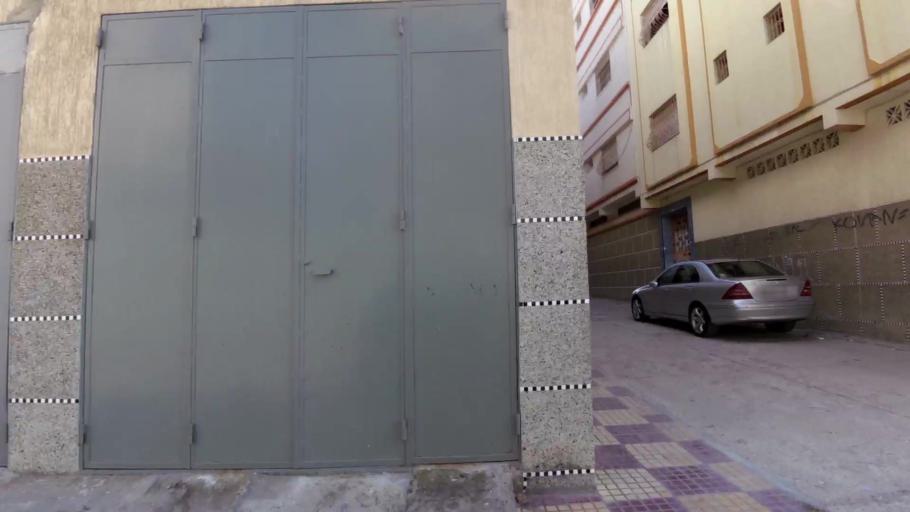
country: MA
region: Tanger-Tetouan
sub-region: Tanger-Assilah
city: Tangier
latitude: 35.7607
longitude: -5.8066
